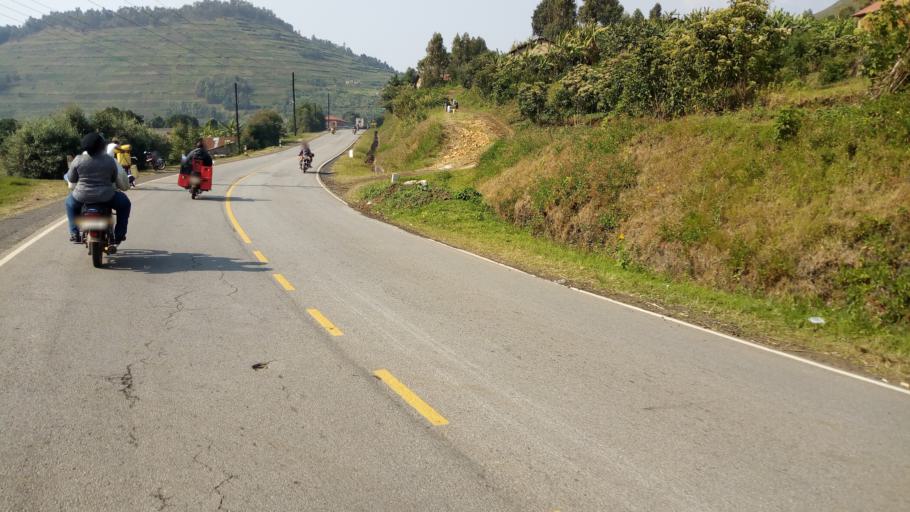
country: UG
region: Western Region
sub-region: Kisoro District
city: Kisoro
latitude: -1.2888
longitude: 29.7099
